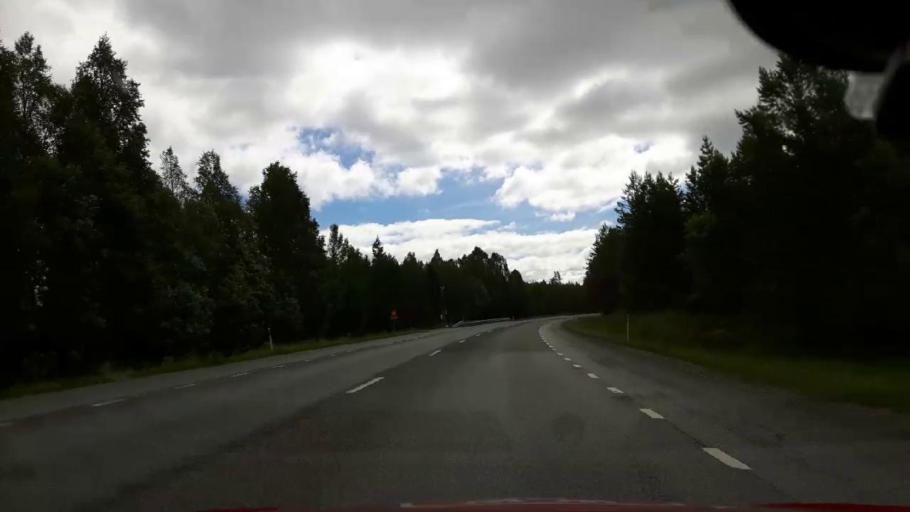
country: SE
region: Jaemtland
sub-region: Braecke Kommun
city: Braecke
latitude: 62.6859
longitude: 15.5799
